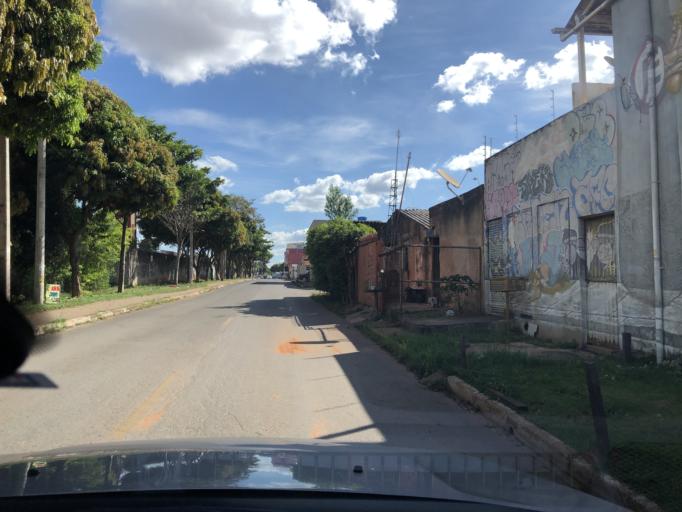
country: BR
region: Federal District
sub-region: Brasilia
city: Brasilia
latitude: -15.7951
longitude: -48.1182
